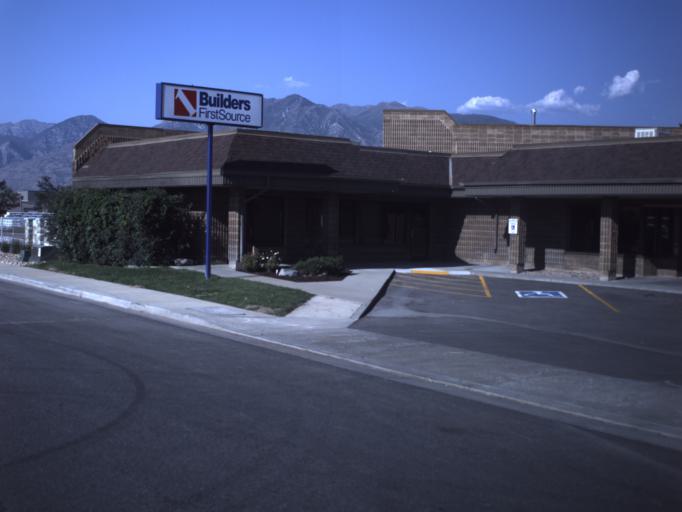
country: US
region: Utah
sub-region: Utah County
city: Spanish Fork
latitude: 40.1275
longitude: -111.6547
